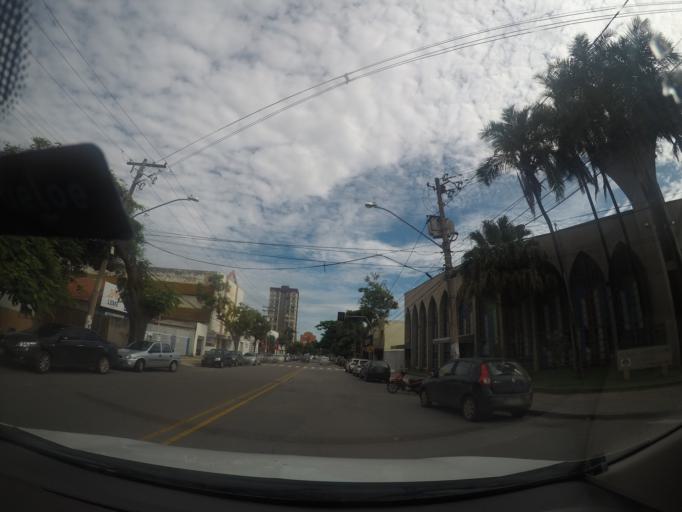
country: BR
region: Goias
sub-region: Goiania
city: Goiania
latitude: -16.6696
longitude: -49.2577
